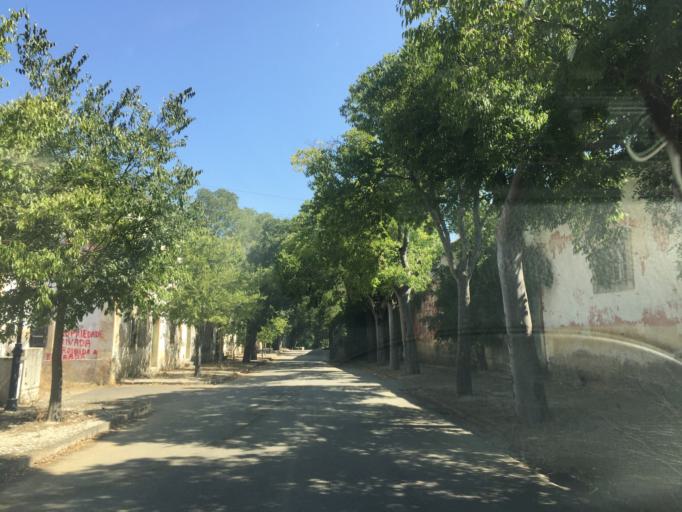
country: PT
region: Santarem
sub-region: Chamusca
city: Vila Nova da Barquinha
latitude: 39.4446
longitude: -8.4503
